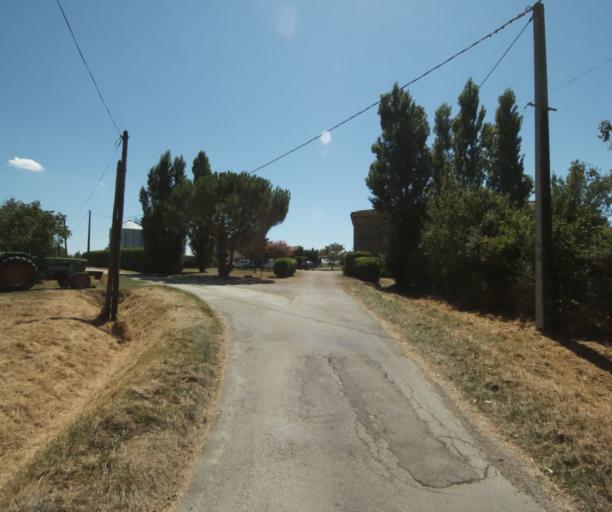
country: FR
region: Midi-Pyrenees
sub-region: Departement de la Haute-Garonne
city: Saint-Felix-Lauragais
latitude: 43.4720
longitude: 1.9413
